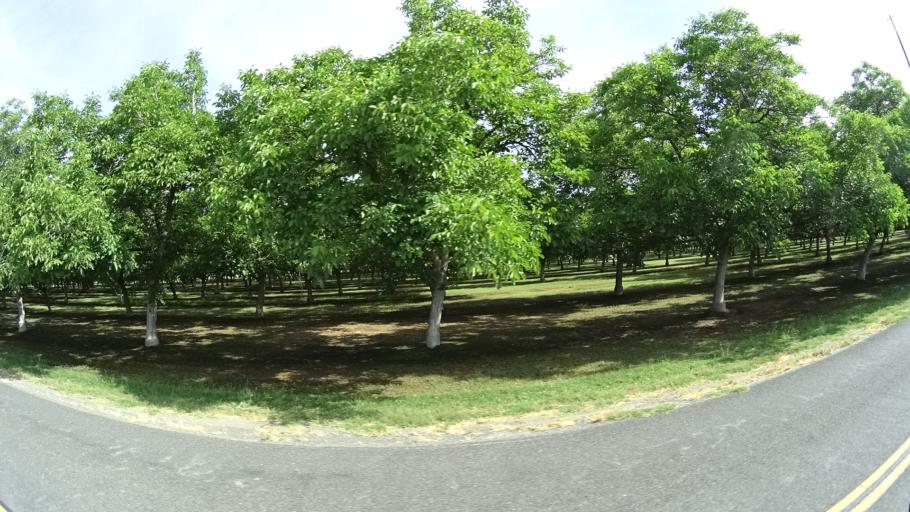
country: US
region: California
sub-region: Fresno County
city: Laton
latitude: 36.4158
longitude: -119.6564
